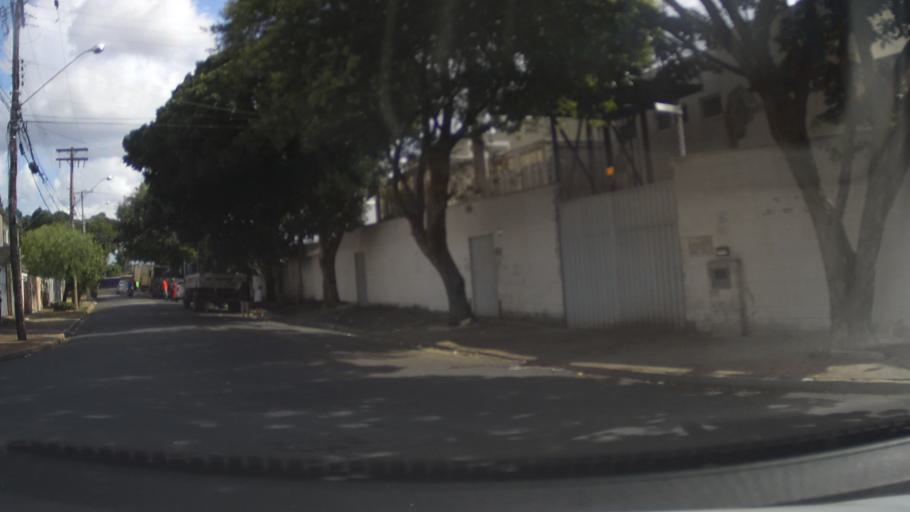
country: BR
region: Sao Paulo
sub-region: Campinas
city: Campinas
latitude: -22.8873
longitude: -47.1120
